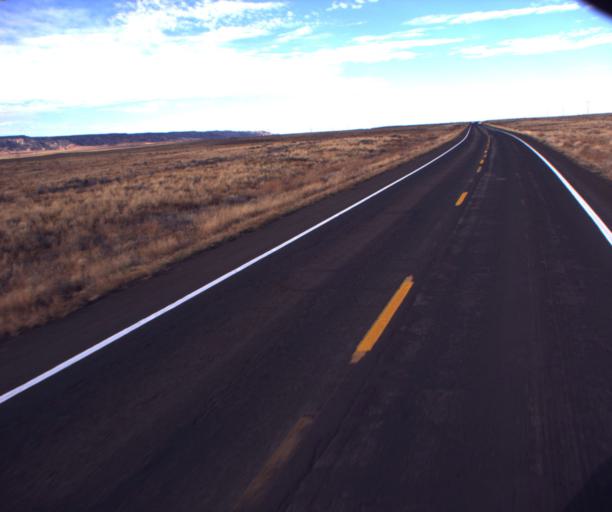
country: US
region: Arizona
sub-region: Apache County
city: Lukachukai
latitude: 36.9584
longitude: -109.3098
